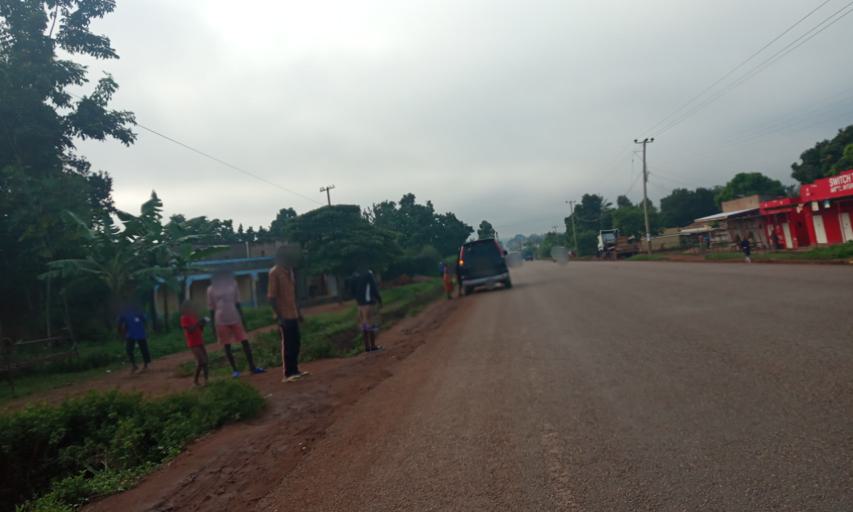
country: UG
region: Eastern Region
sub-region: Mbale District
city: Mbale
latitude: 1.1199
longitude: 34.1697
